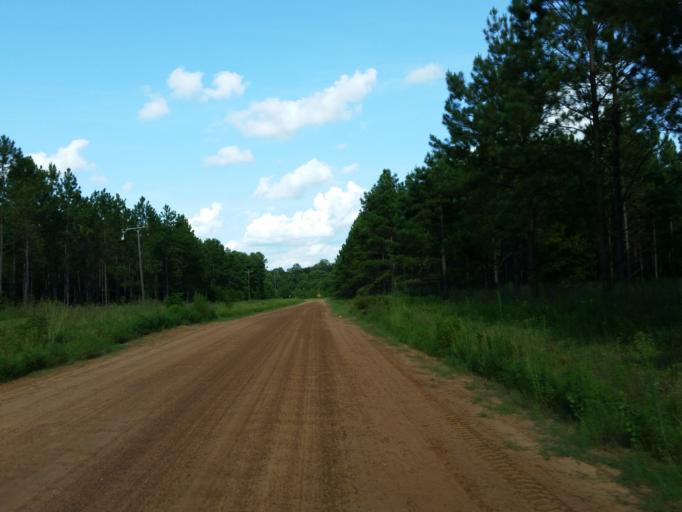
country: US
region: Georgia
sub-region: Lee County
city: Leesburg
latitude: 31.9044
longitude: -84.0694
